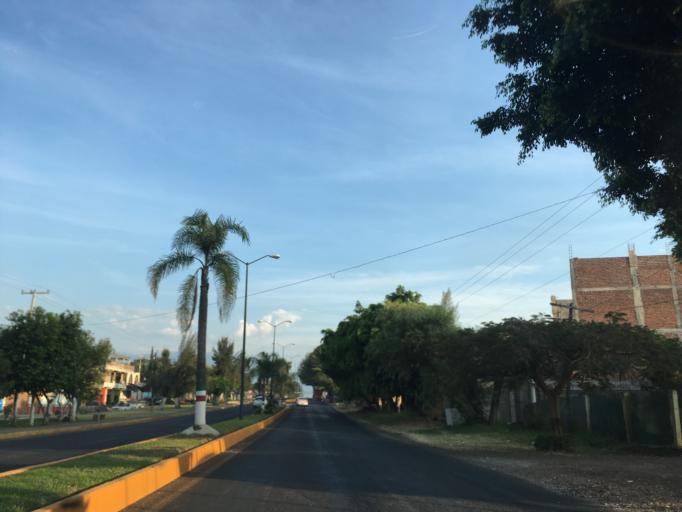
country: MX
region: Michoacan
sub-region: Los Reyes
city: La Higuerita (Colonia San Rafael)
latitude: 19.6173
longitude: -102.4848
